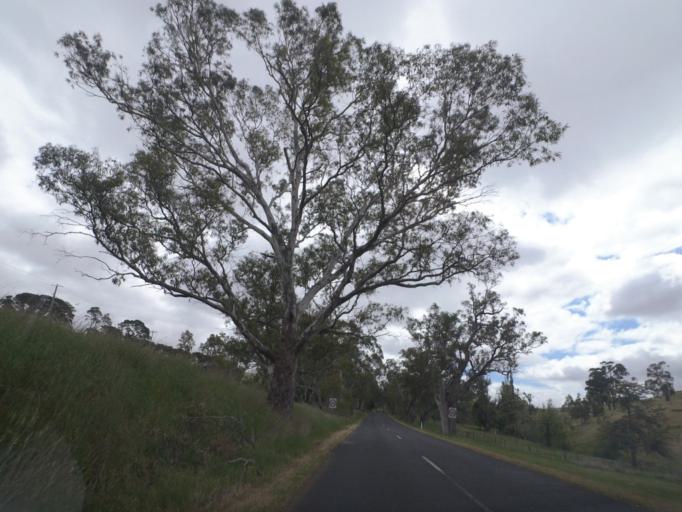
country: AU
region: Victoria
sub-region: Whittlesea
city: Whittlesea
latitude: -37.1969
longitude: 145.0381
